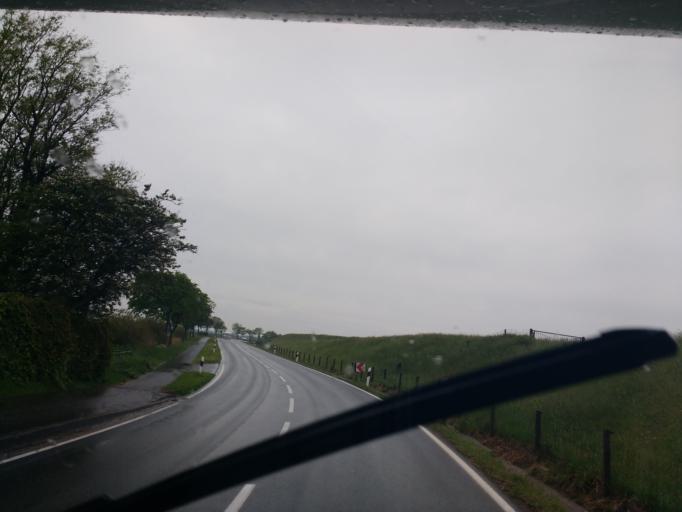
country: DE
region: Lower Saxony
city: Neuharlingersiel
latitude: 53.6959
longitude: 7.7331
